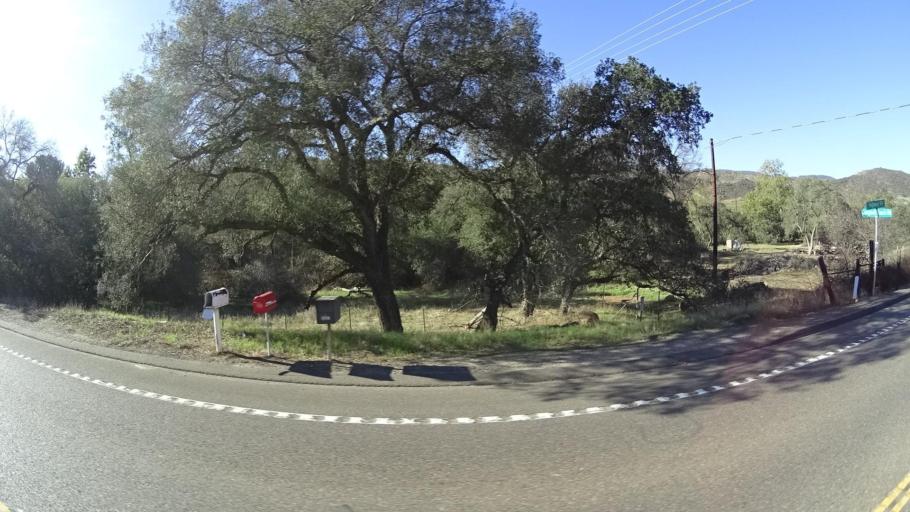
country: US
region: California
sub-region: San Diego County
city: Jamul
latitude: 32.6424
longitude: -116.7752
